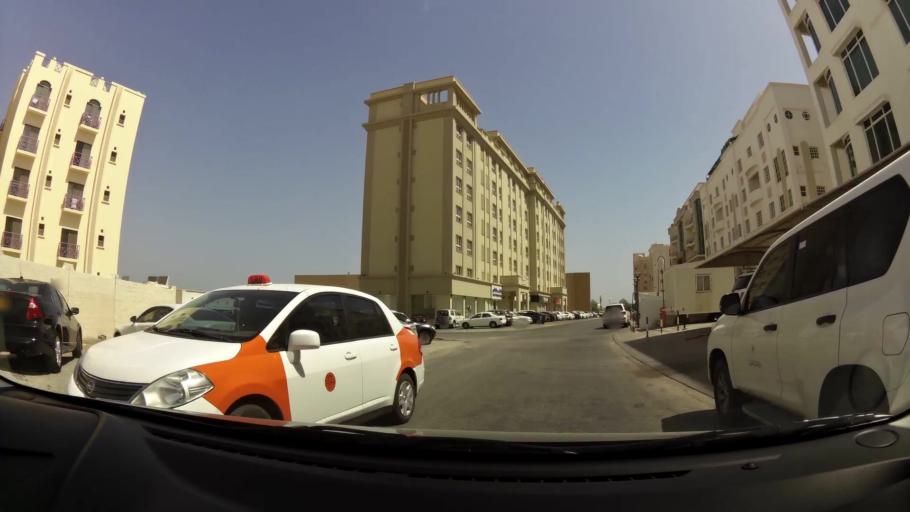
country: OM
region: Muhafazat Masqat
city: Bawshar
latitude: 23.5944
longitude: 58.4473
